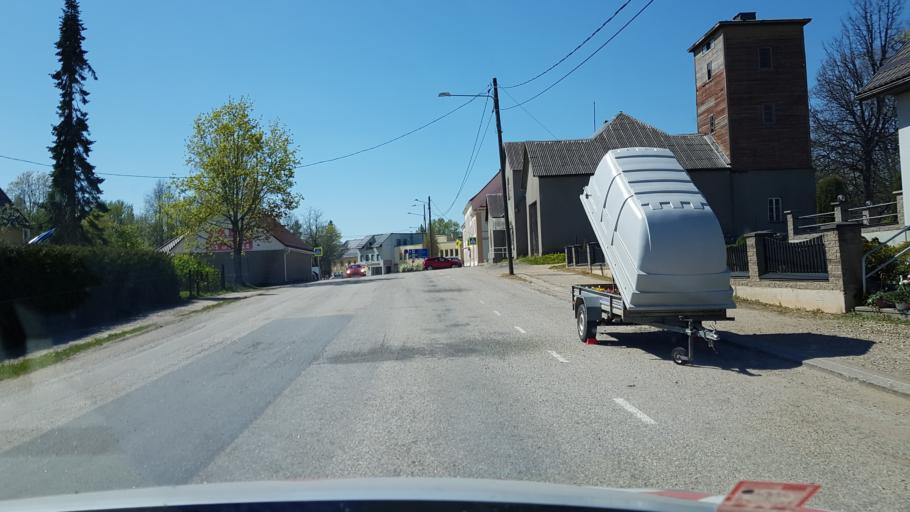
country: EE
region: Vorumaa
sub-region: Antsla vald
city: Vana-Antsla
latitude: 57.8296
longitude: 26.5307
